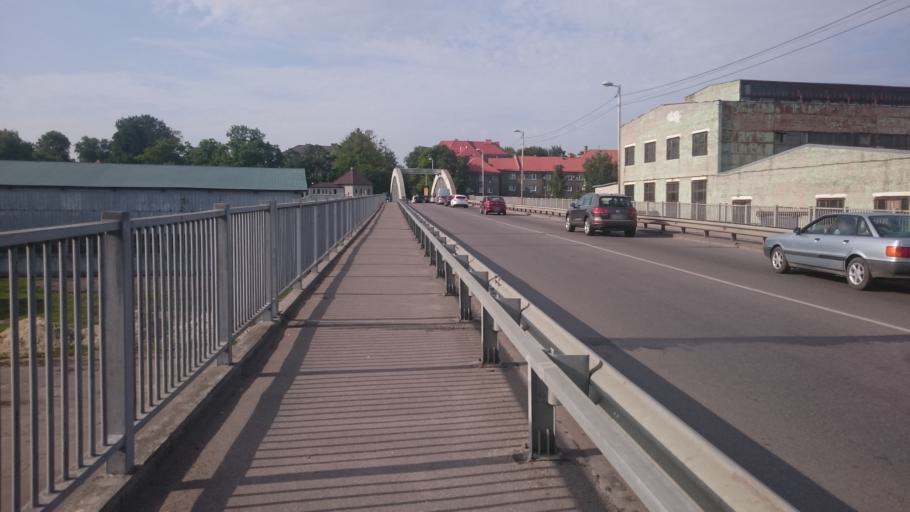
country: RU
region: Kaliningrad
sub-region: Gorod Kaliningrad
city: Kaliningrad
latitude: 54.7095
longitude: 20.4586
